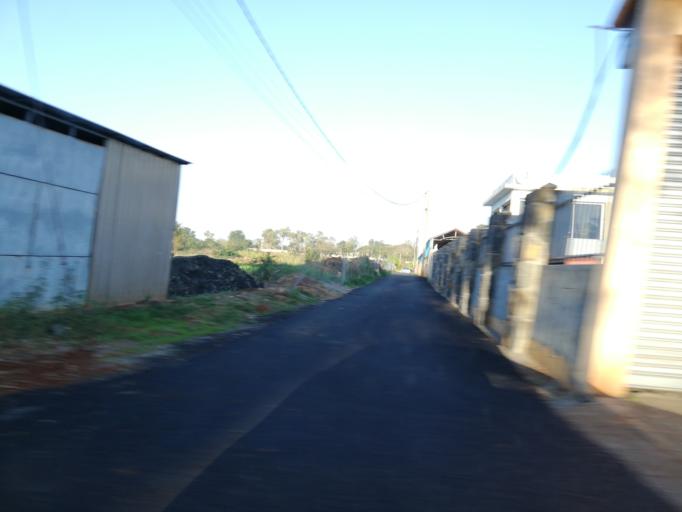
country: MU
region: Pamplemousses
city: Terre Rouge
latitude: -20.1215
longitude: 57.5317
